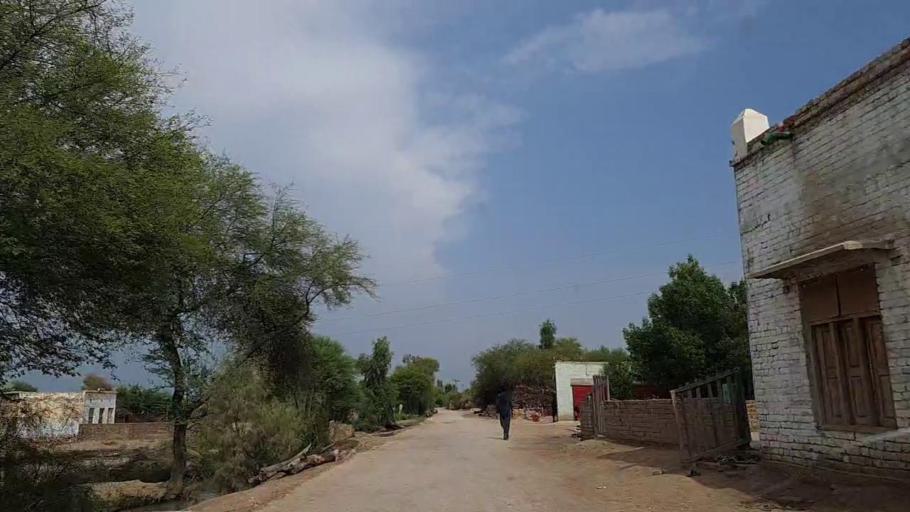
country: PK
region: Sindh
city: Khanpur
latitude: 27.8391
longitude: 69.4805
